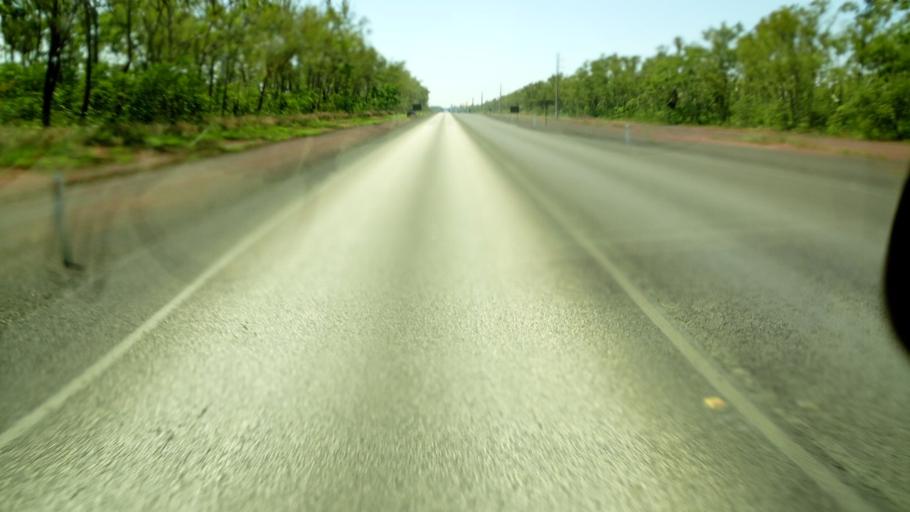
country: AU
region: Northern Territory
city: Alyangula
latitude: -13.9602
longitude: 136.4429
